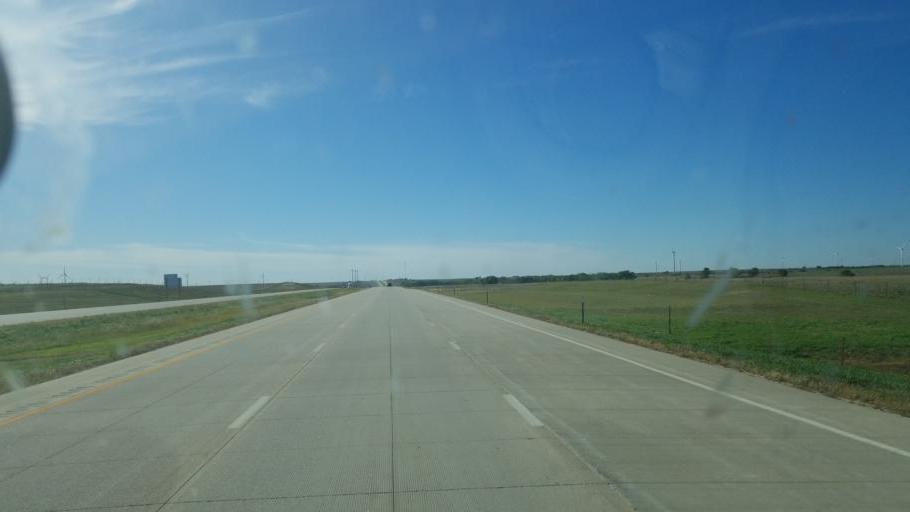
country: US
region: Kansas
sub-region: Ellsworth County
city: Ellsworth
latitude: 38.8494
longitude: -98.2839
